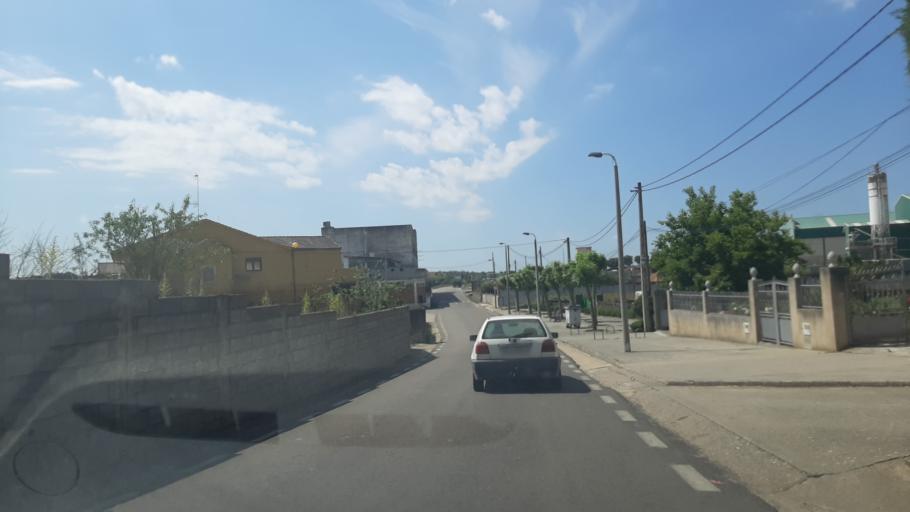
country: ES
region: Castille and Leon
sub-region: Provincia de Salamanca
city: Gallegos de Arganan
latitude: 40.6277
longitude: -6.7037
